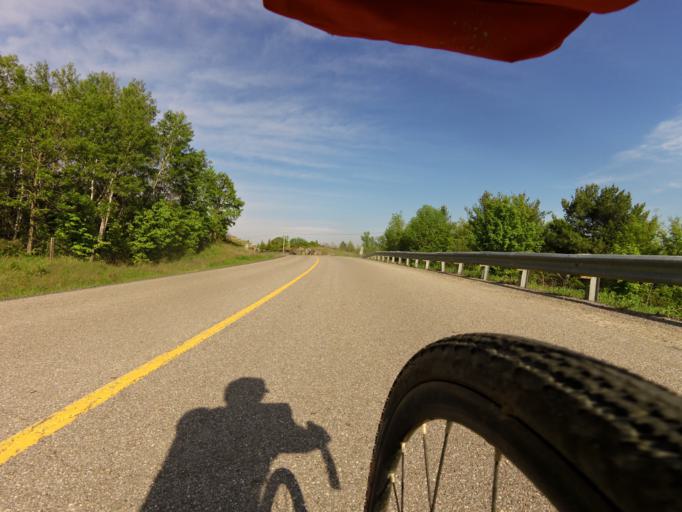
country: CA
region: Ontario
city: Arnprior
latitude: 45.1665
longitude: -76.4830
